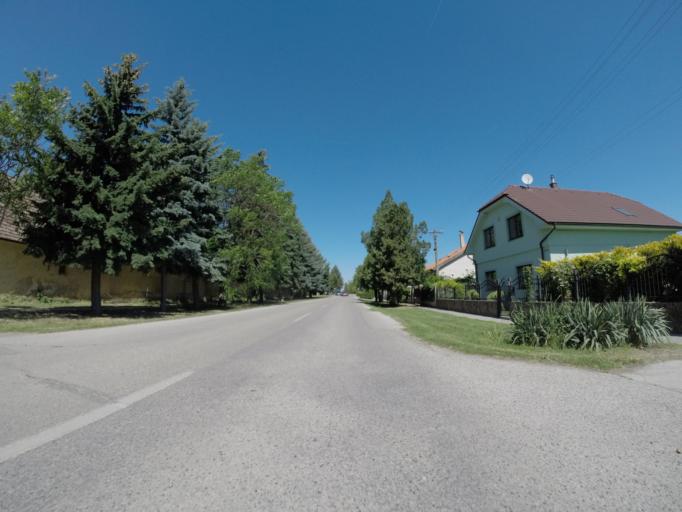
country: SK
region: Trnavsky
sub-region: Okres Galanta
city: Galanta
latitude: 48.2024
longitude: 17.7116
